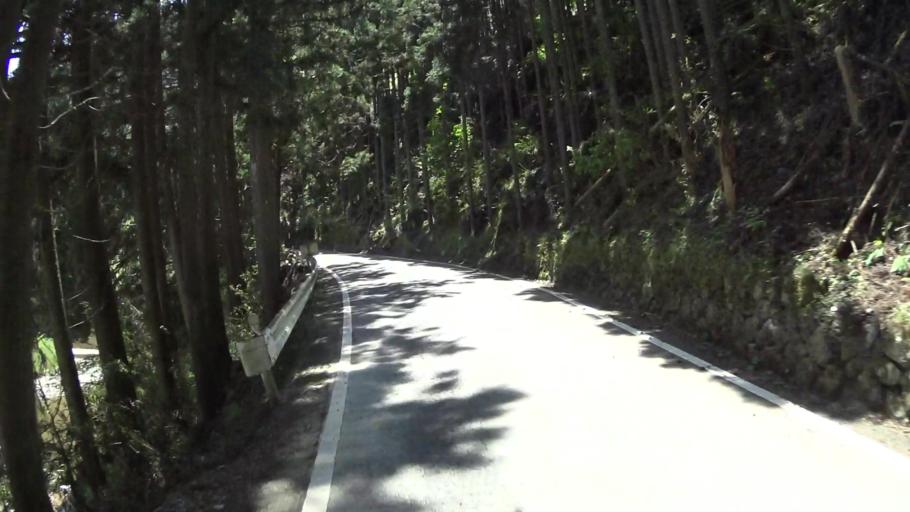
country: JP
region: Kyoto
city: Kameoka
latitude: 35.1380
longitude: 135.5860
